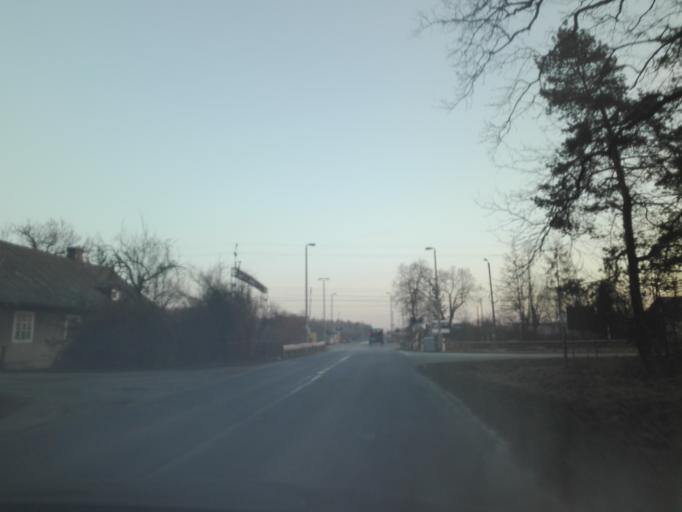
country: PL
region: Subcarpathian Voivodeship
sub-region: Powiat tarnobrzeski
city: Sokolniki
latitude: 50.6049
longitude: 21.8368
